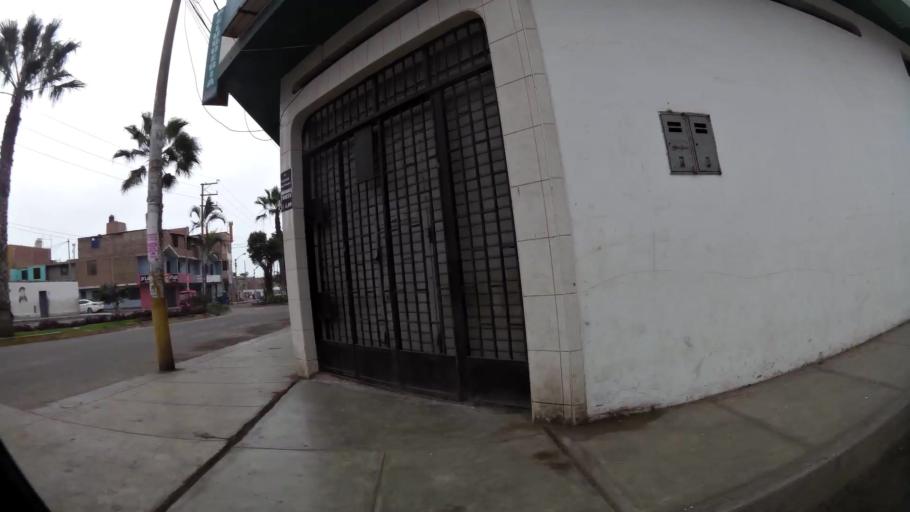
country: PE
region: Lima
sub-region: Barranca
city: Barranca
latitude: -10.7493
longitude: -77.7547
